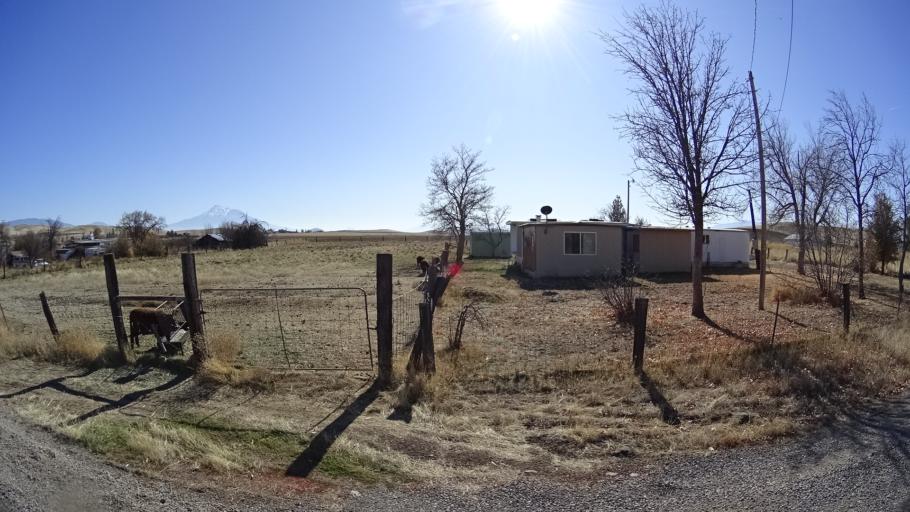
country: US
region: California
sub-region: Siskiyou County
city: Montague
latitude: 41.7557
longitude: -122.4627
